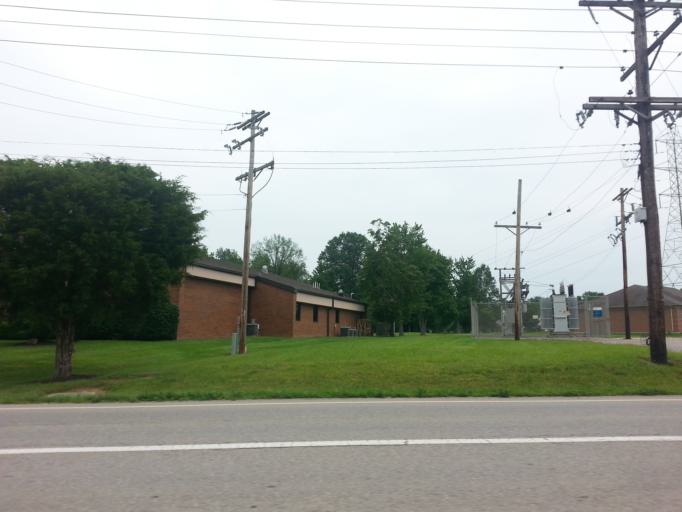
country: US
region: Ohio
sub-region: Brown County
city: Mount Orab
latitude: 39.0185
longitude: -83.9241
